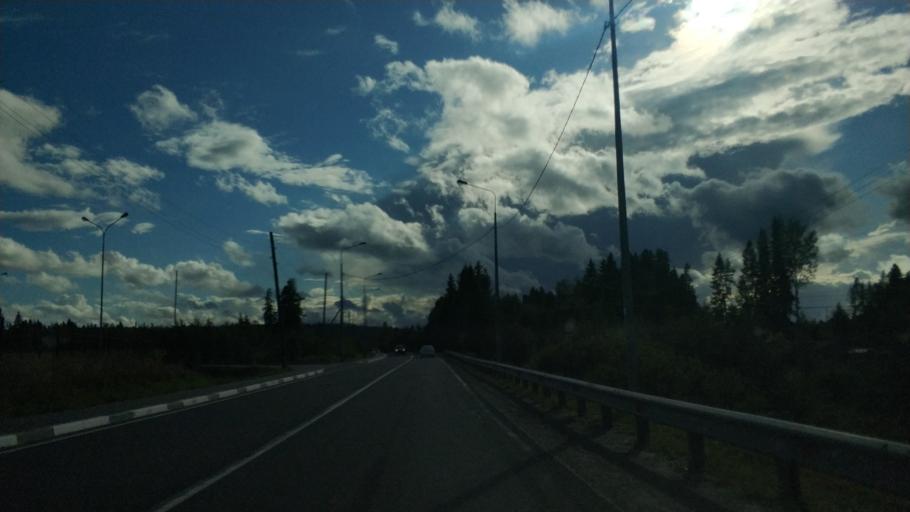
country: RU
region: Republic of Karelia
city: Lakhdenpokh'ya
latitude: 61.5222
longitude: 30.1597
